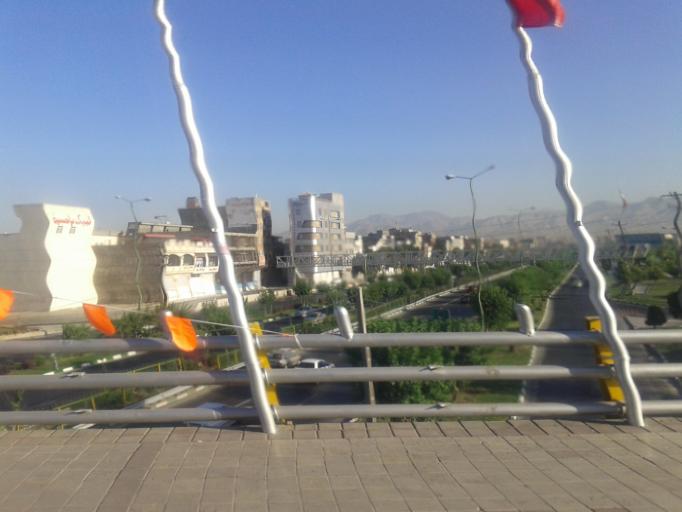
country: IR
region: Tehran
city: Rey
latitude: 35.6279
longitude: 51.3609
